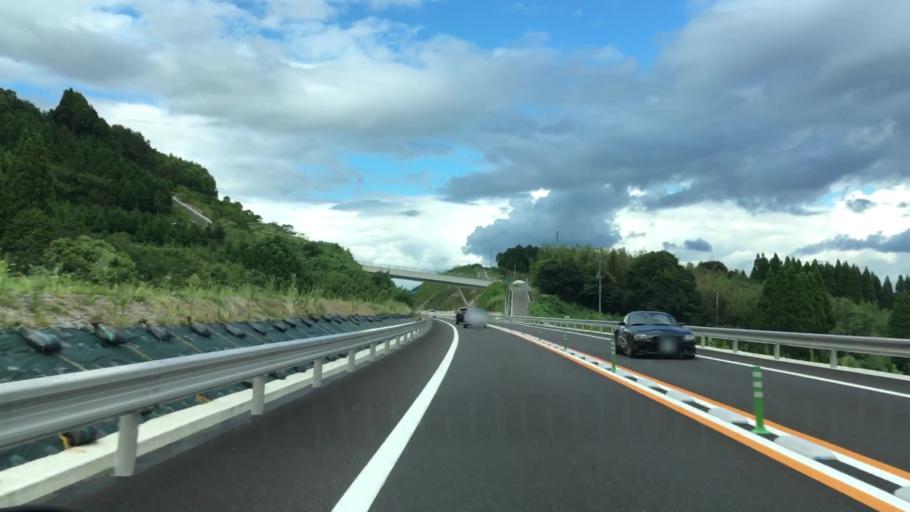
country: JP
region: Saga Prefecture
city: Imaricho-ko
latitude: 33.3195
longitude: 129.9248
